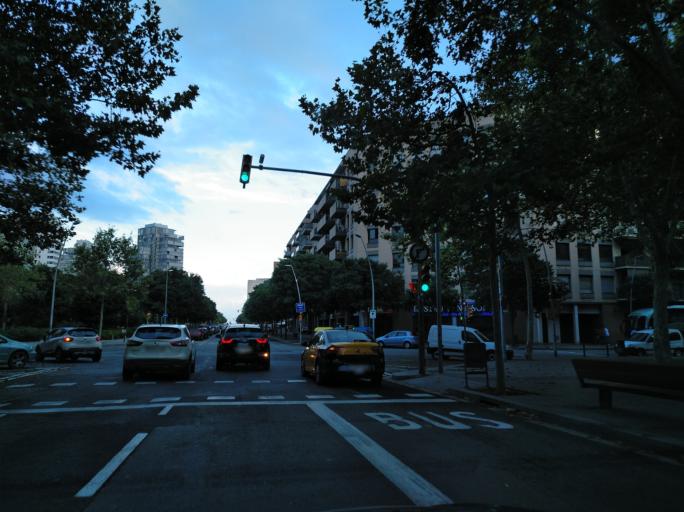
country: ES
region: Catalonia
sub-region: Provincia de Barcelona
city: Sant Marti
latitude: 41.4078
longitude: 2.2105
